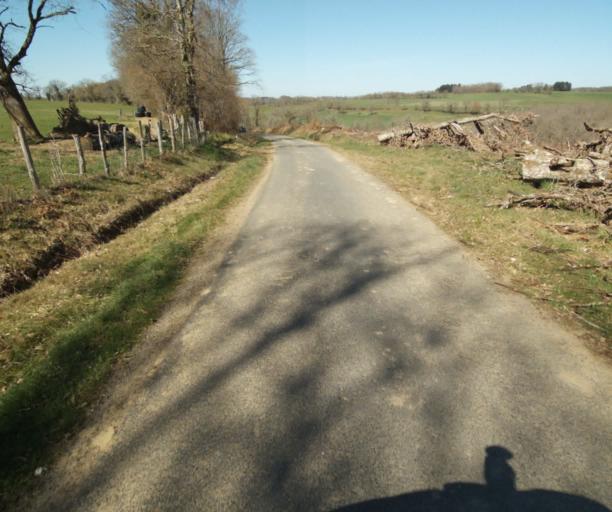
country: FR
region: Limousin
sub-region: Departement de la Correze
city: Chamboulive
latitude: 45.4500
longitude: 1.6941
